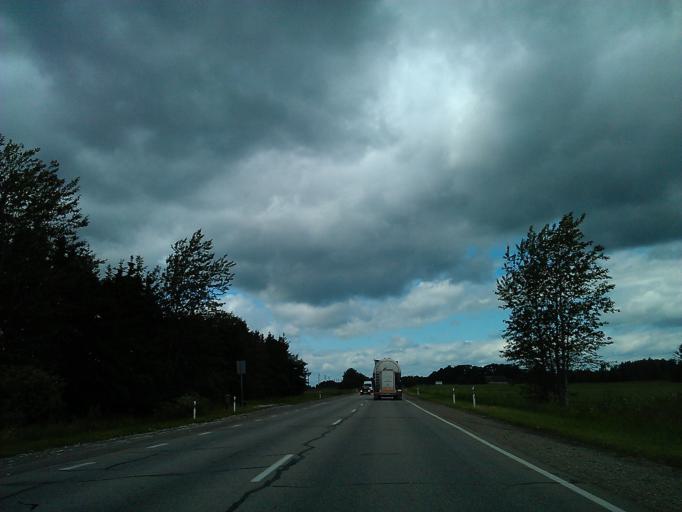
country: LV
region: Tukuma Rajons
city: Tukums
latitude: 56.9250
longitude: 23.2368
